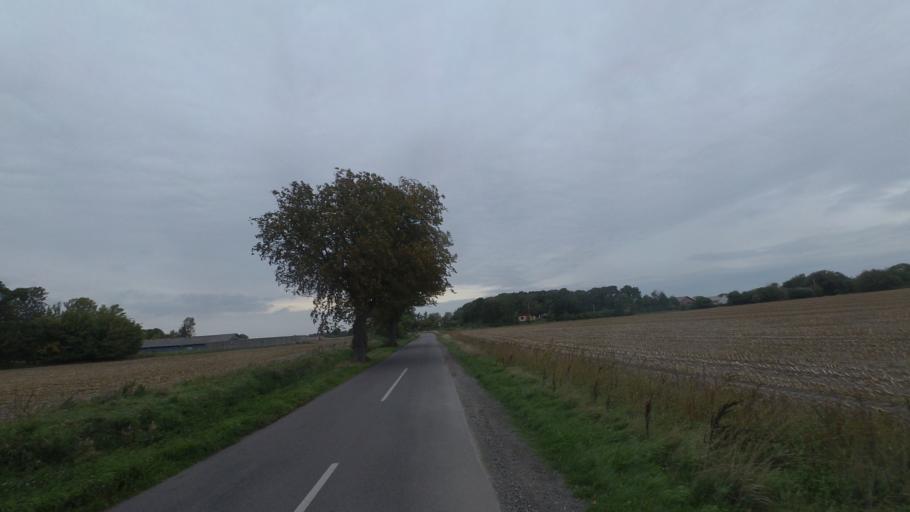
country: DK
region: Capital Region
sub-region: Bornholm Kommune
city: Akirkeby
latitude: 55.0075
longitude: 14.9914
